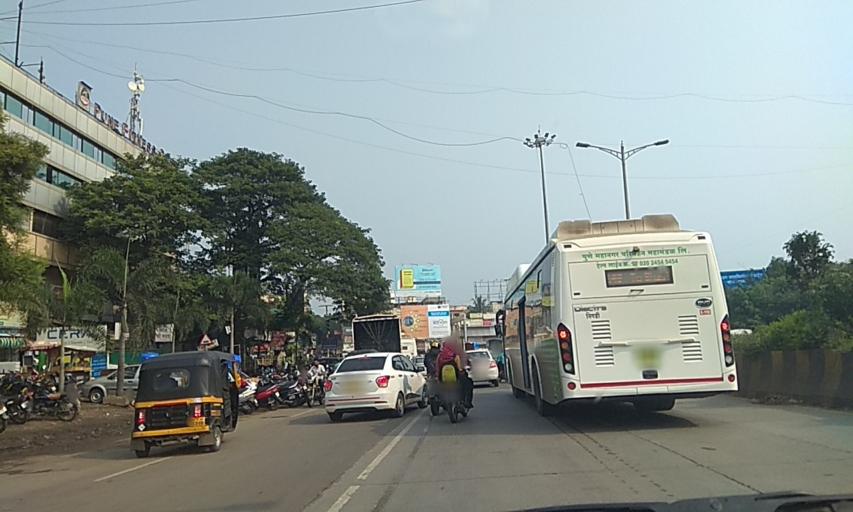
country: IN
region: Maharashtra
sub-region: Pune Division
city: Lohogaon
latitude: 18.5614
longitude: 73.9385
